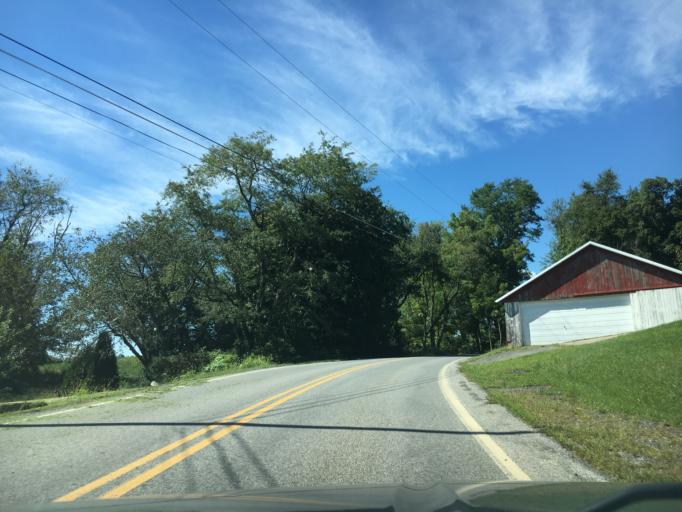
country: US
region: Pennsylvania
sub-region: Berks County
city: Topton
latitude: 40.5348
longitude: -75.6833
